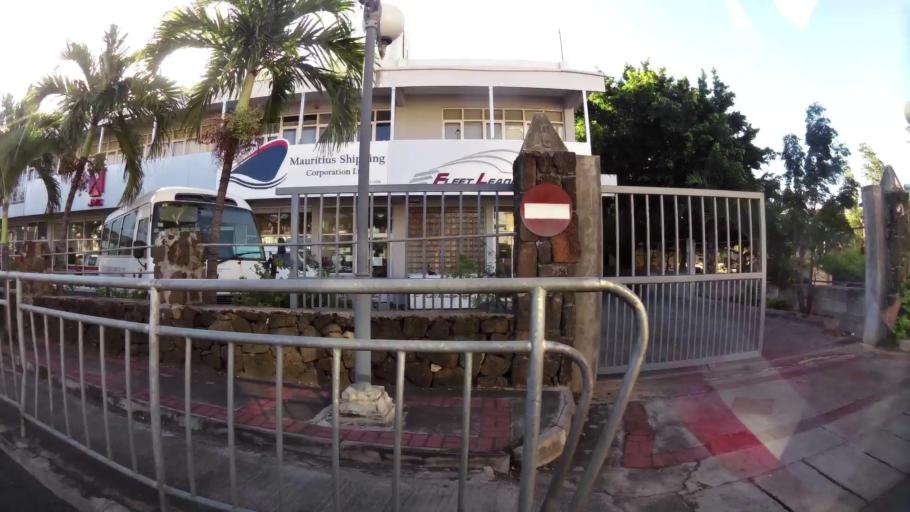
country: MU
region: Port Louis
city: Port Louis
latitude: -20.1529
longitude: 57.5089
